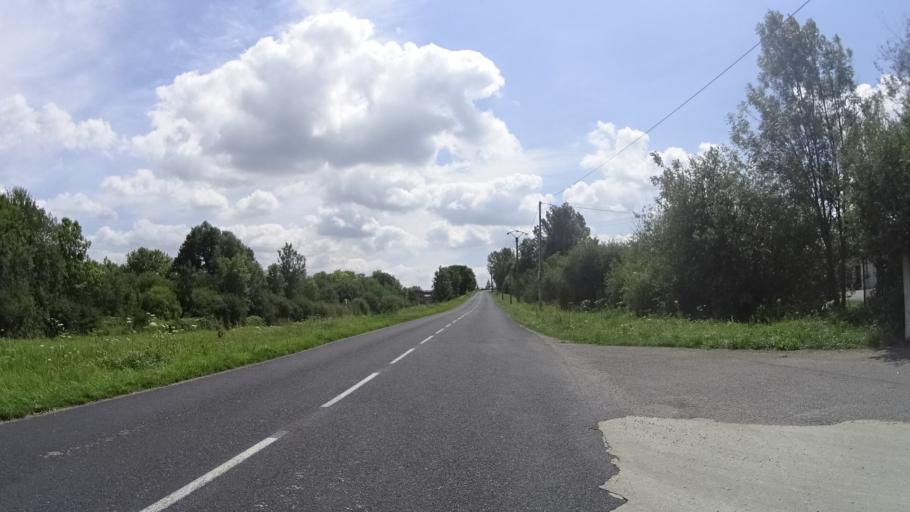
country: FR
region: Lorraine
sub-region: Departement de la Meuse
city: Euville
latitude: 48.7216
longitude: 5.6653
